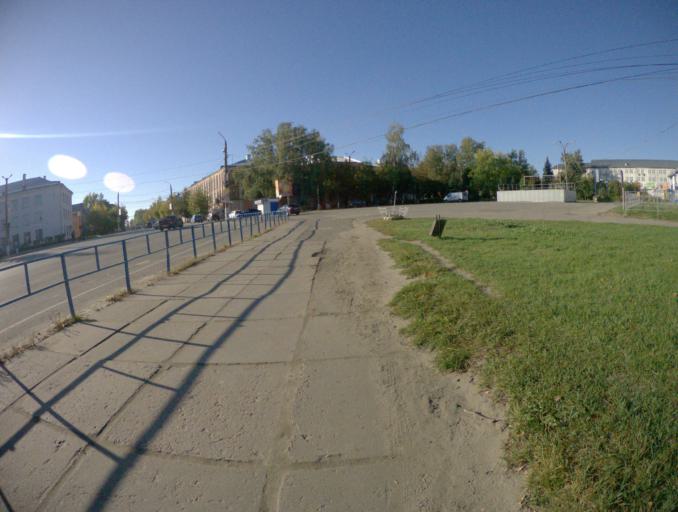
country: RU
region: Vladimir
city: Sobinka
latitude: 55.9938
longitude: 40.0181
